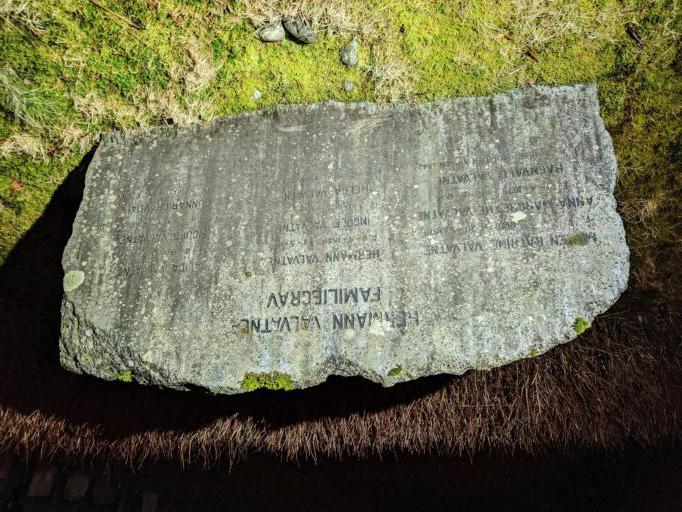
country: NO
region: Rogaland
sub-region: Vindafjord
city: Olen
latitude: 59.8669
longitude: 5.7586
